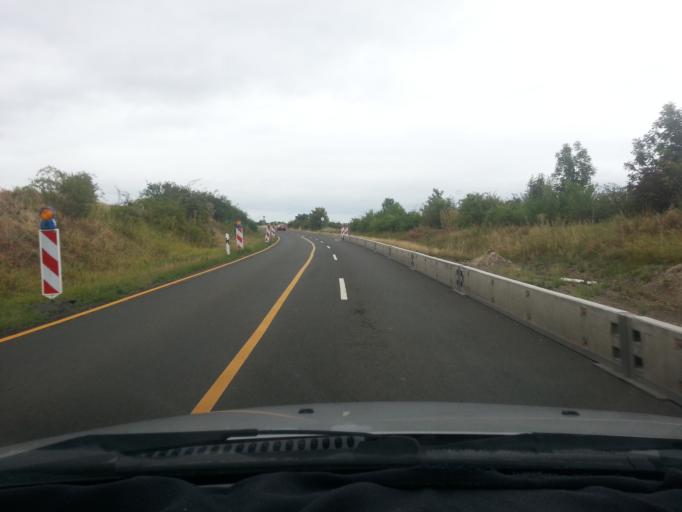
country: DE
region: Rheinland-Pfalz
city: Wachenheim
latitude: 49.4533
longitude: 8.1857
